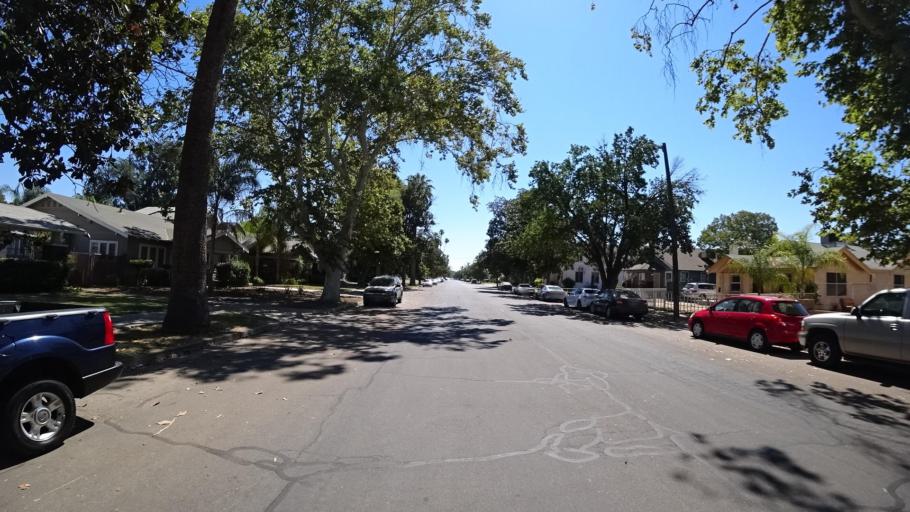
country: US
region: California
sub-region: Fresno County
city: Fresno
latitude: 36.7381
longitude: -119.7688
